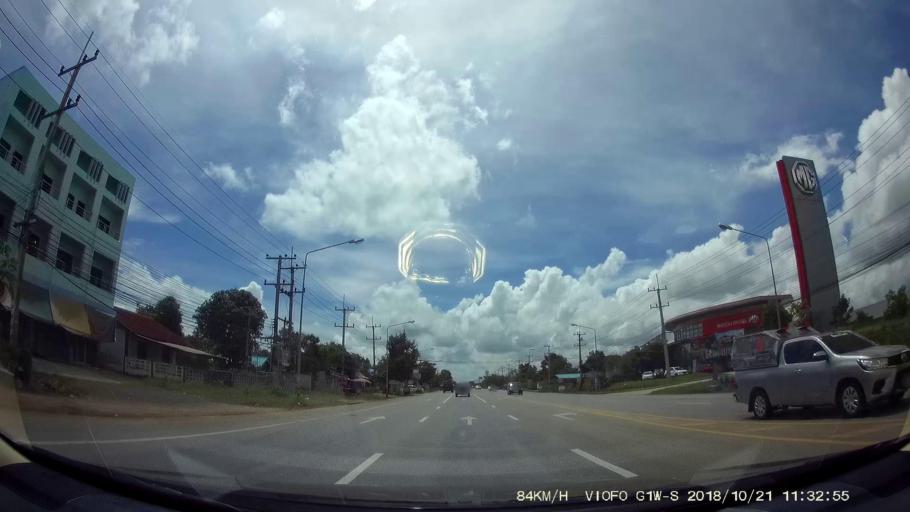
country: TH
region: Chaiyaphum
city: Chaiyaphum
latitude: 15.7519
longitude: 102.0240
